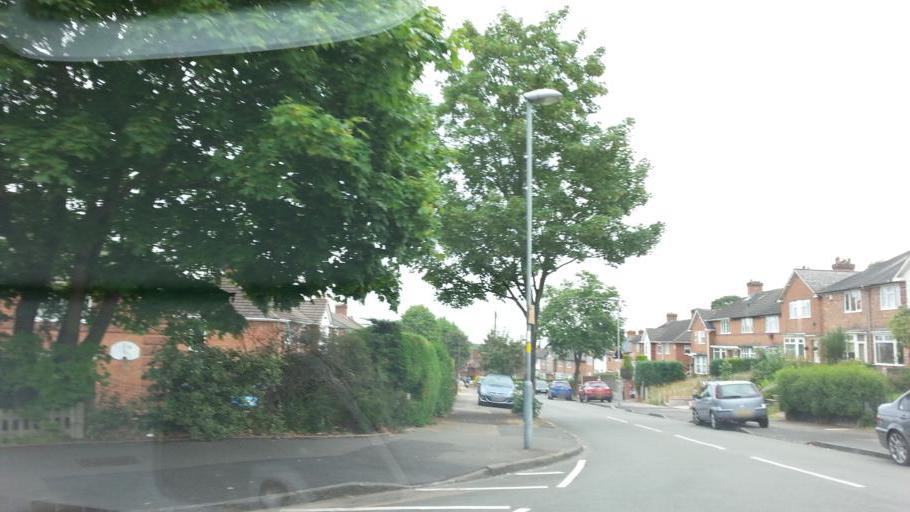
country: GB
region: England
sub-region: Worcestershire
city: Barnt Green
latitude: 52.3935
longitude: -2.0043
